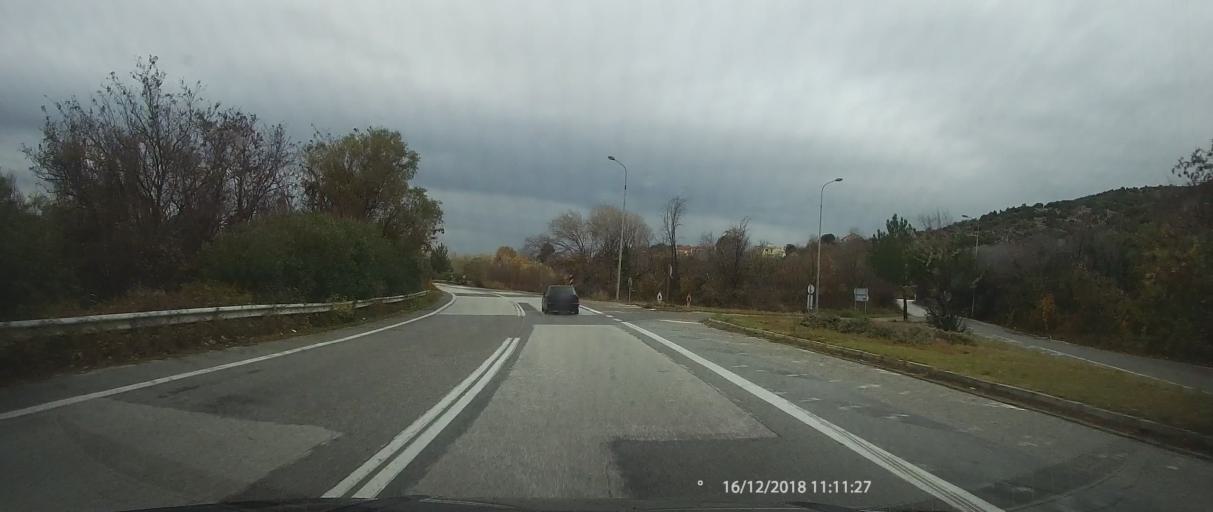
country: GR
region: East Macedonia and Thrace
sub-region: Nomos Xanthis
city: Petrochori
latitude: 41.0855
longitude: 24.7641
